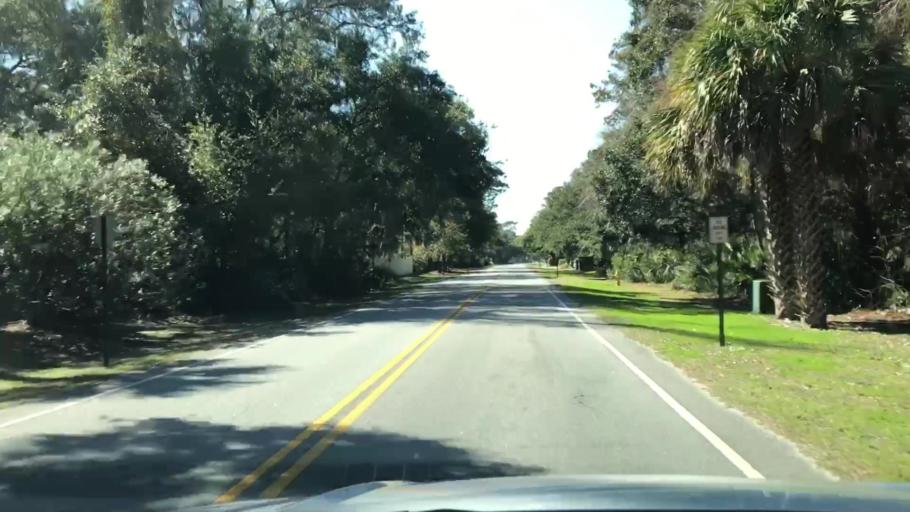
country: US
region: South Carolina
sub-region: Beaufort County
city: Hilton Head Island
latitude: 32.1452
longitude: -80.7454
